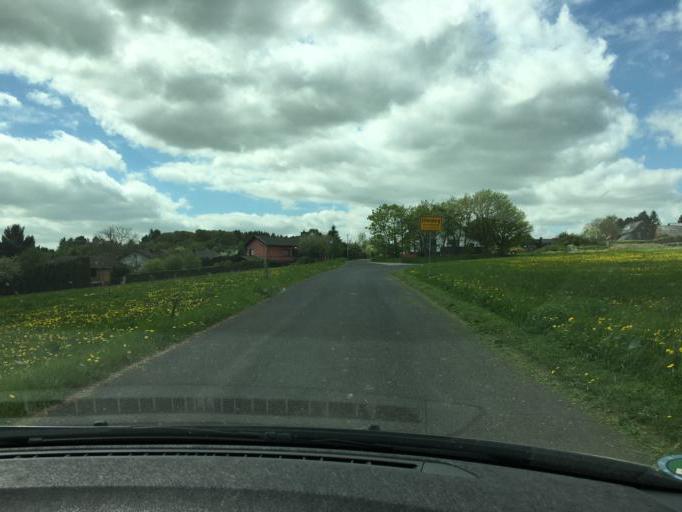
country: DE
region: Rheinland-Pfalz
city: Kirchsahr
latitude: 50.5170
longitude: 6.8756
